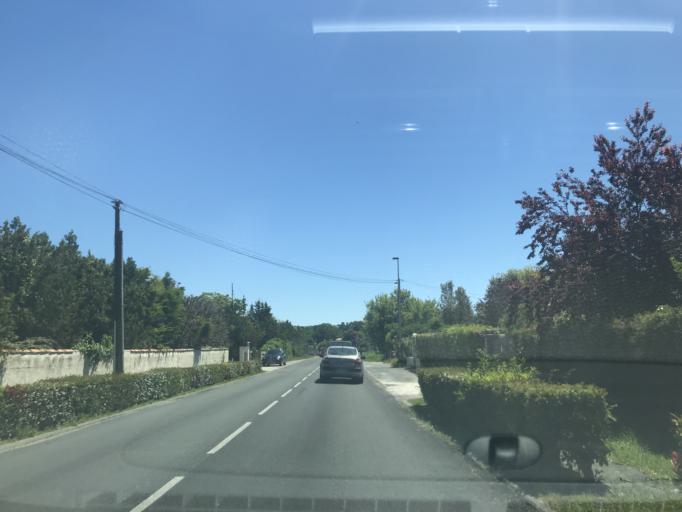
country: FR
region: Poitou-Charentes
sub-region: Departement de la Charente-Maritime
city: Meschers-sur-Gironde
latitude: 45.5727
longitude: -0.9611
